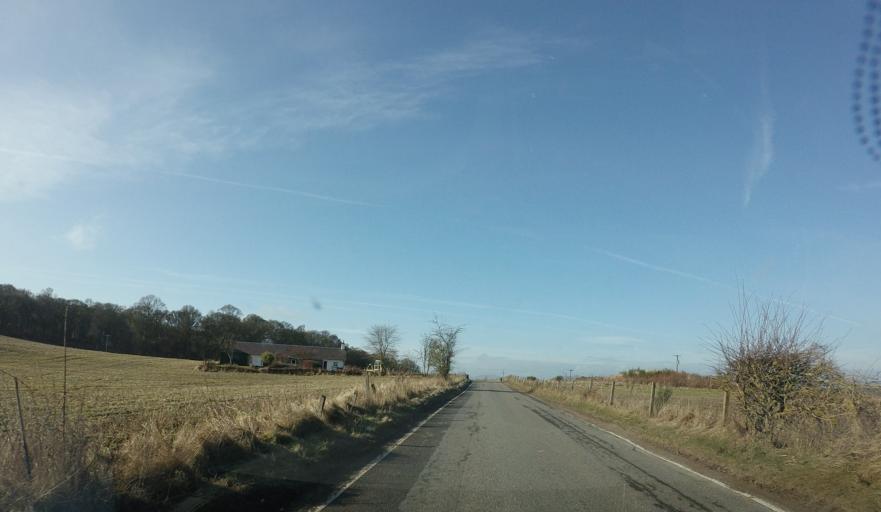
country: GB
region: Scotland
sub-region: Perth and Kinross
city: Stanley
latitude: 56.5286
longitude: -3.3924
